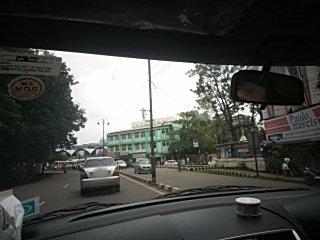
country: IN
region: Goa
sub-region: North Goa
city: Panaji
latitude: 15.4973
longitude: 73.8361
